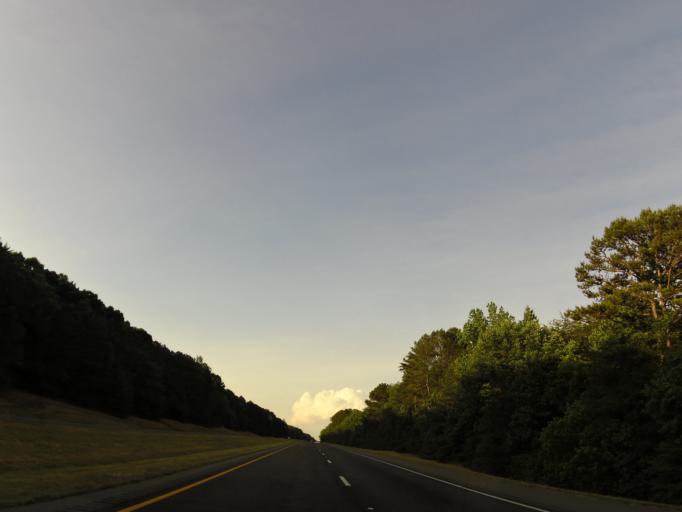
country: US
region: Alabama
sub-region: DeKalb County
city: Henagar
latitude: 34.5712
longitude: -85.6608
